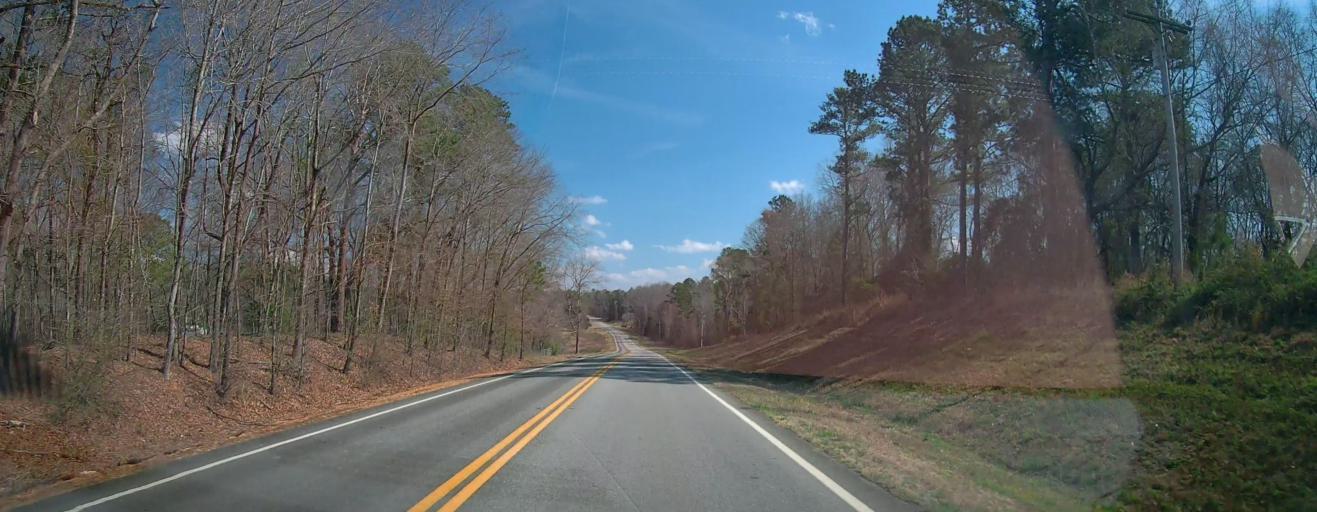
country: US
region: Georgia
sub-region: Wilkinson County
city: Gordon
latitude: 32.9043
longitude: -83.3748
